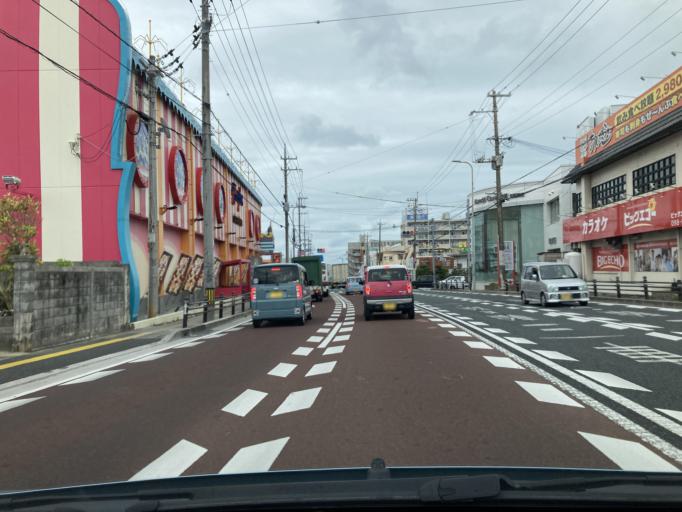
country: JP
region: Okinawa
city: Ginowan
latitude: 26.1999
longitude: 127.7489
